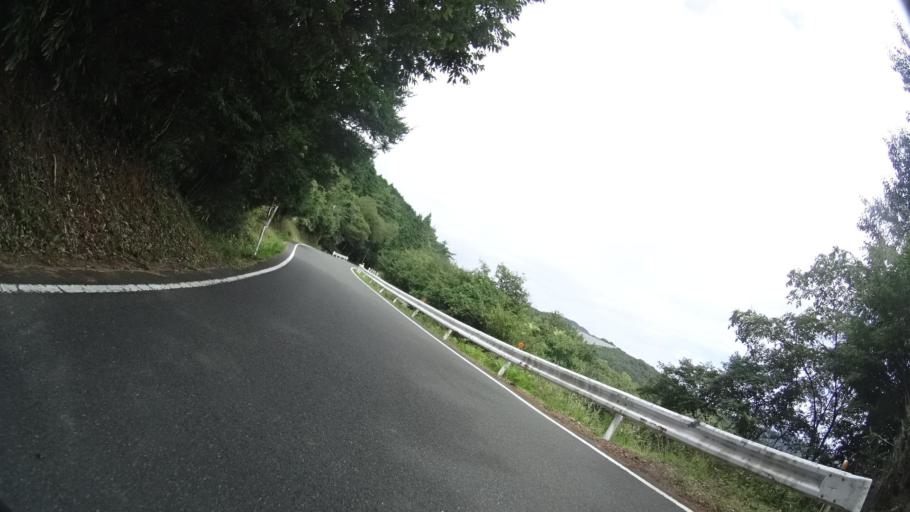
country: JP
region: Kyoto
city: Miyazu
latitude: 35.4736
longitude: 135.1575
